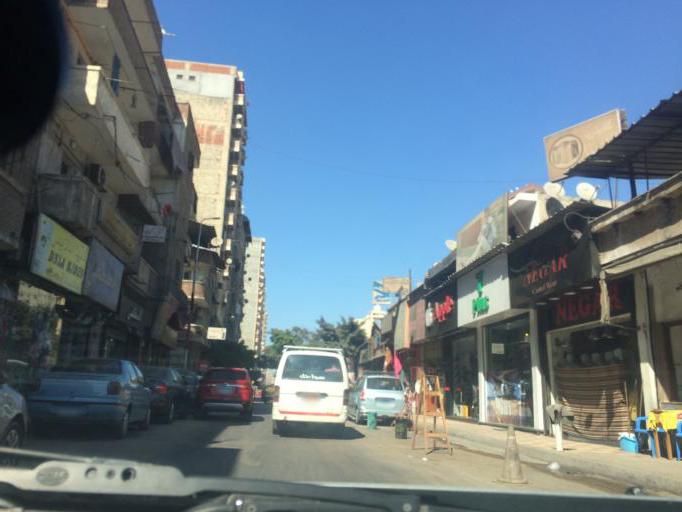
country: EG
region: Alexandria
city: Alexandria
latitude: 31.2521
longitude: 29.9854
